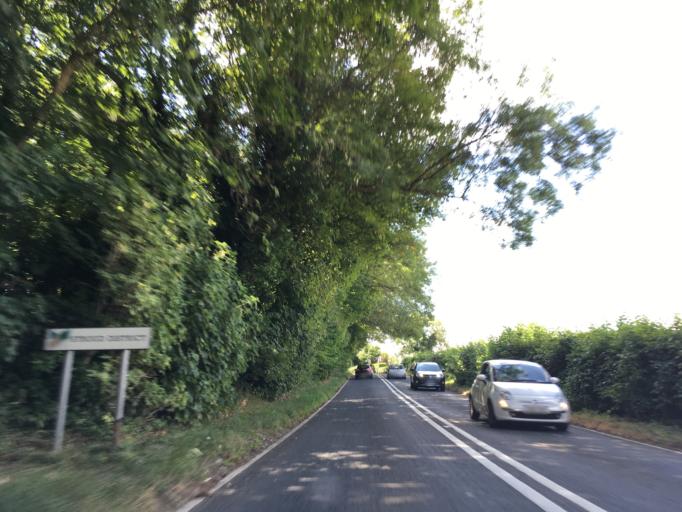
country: GB
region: England
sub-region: Gloucestershire
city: Churchdown
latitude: 51.8294
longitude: -2.1667
